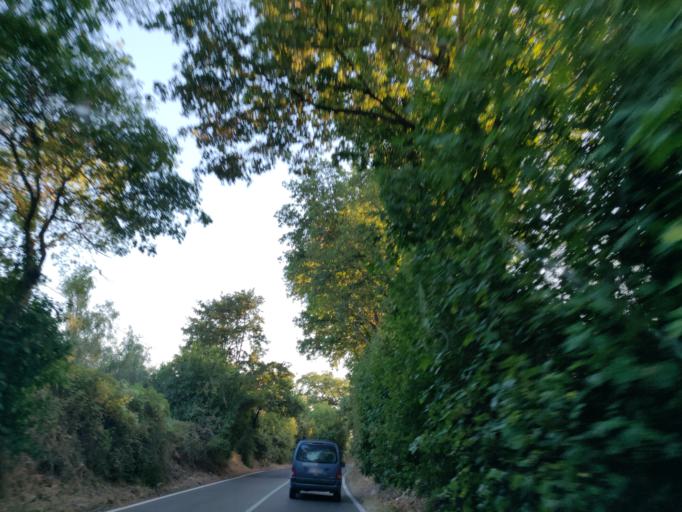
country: IT
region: Latium
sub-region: Provincia di Viterbo
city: Canino
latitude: 42.4413
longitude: 11.7306
